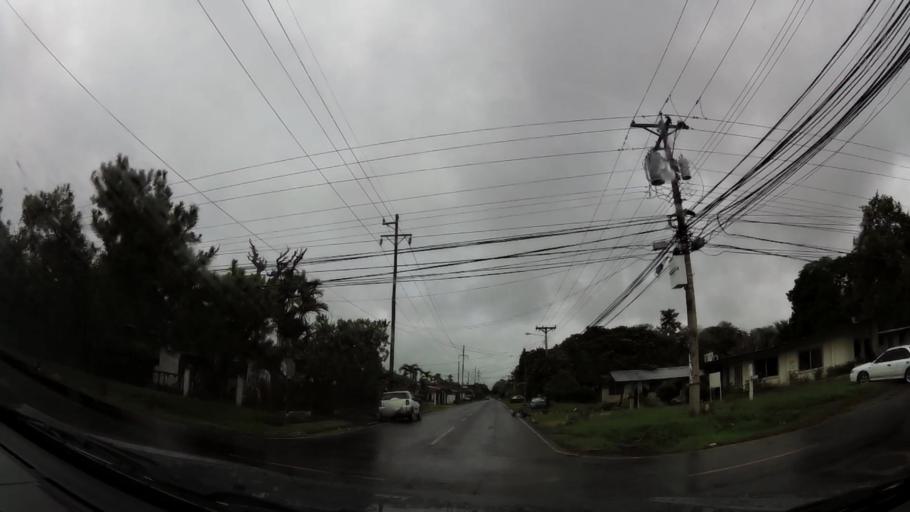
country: PA
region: Chiriqui
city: David
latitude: 8.4353
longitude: -82.4325
